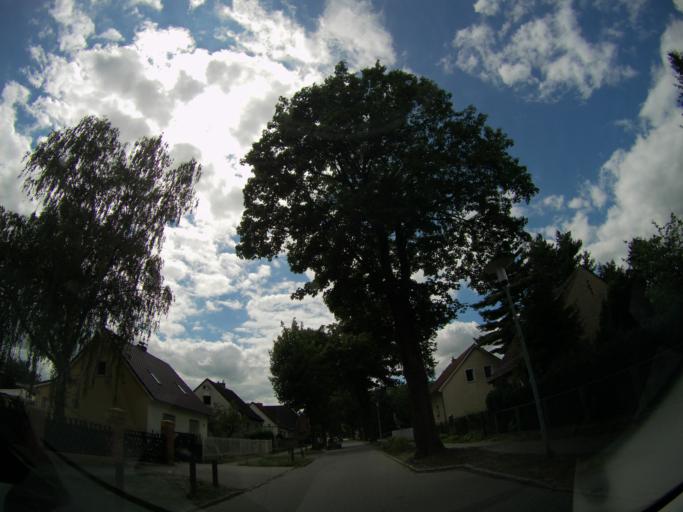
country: DE
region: Brandenburg
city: Teltow
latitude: 52.3969
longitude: 13.2868
